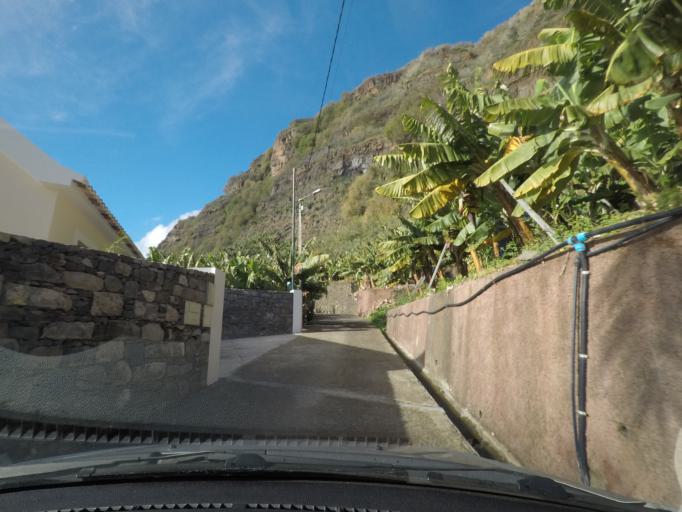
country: PT
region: Madeira
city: Ponta do Sol
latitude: 32.6890
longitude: -17.1169
